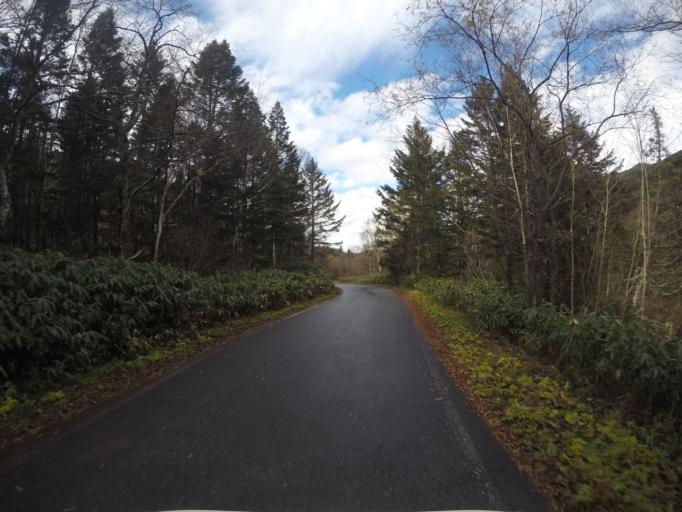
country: JP
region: Gifu
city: Takayama
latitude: 36.1827
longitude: 137.5773
